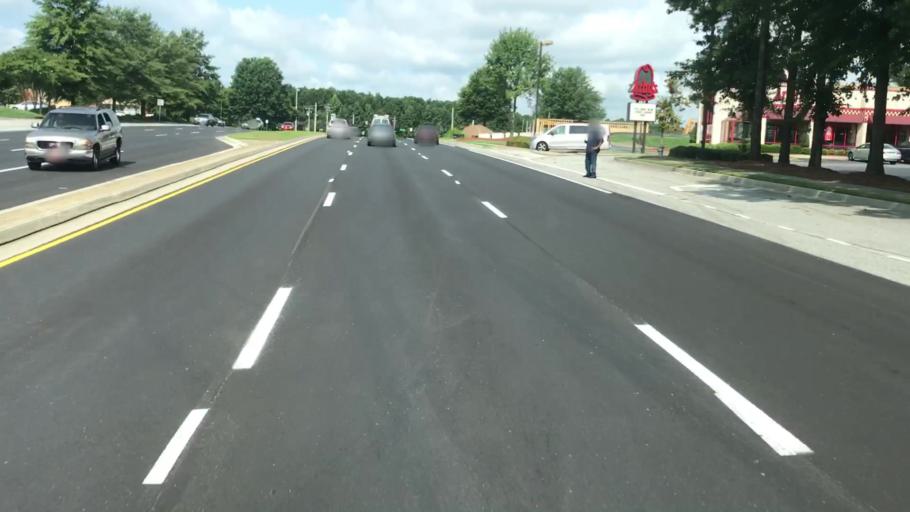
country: US
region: Georgia
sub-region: Gwinnett County
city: Lawrenceville
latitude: 33.9551
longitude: -84.0537
